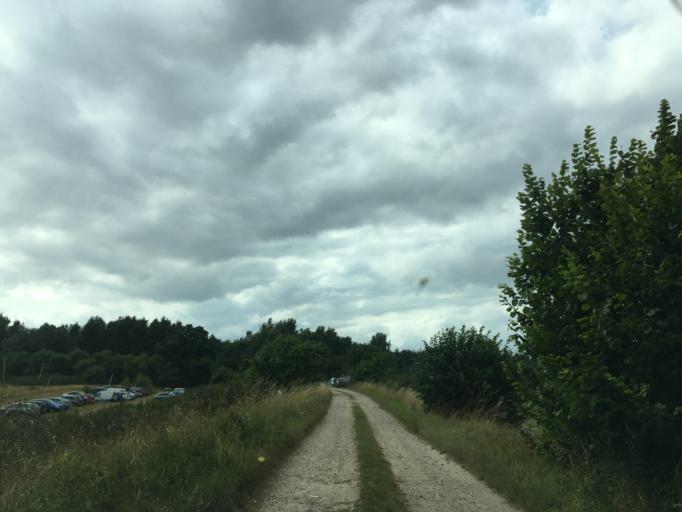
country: DK
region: South Denmark
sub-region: Middelfart Kommune
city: Ejby
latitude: 55.3895
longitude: 9.9461
